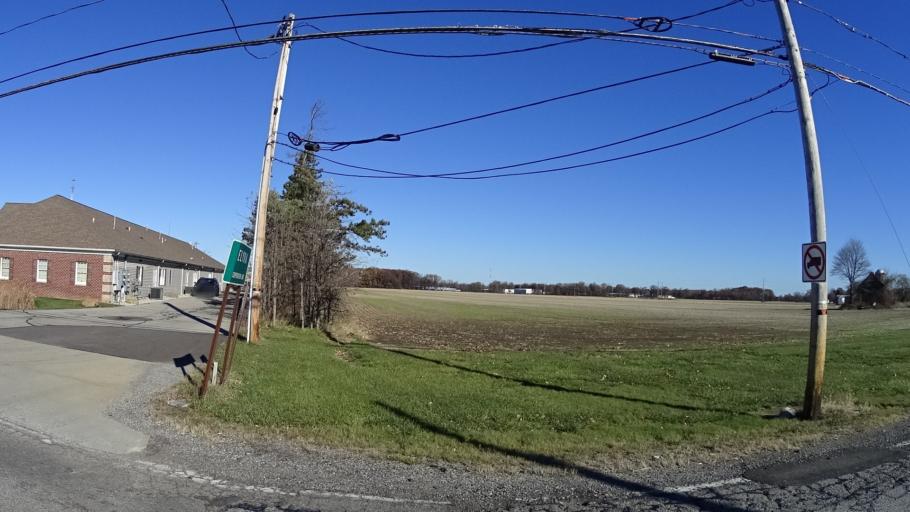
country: US
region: Ohio
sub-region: Lorain County
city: Elyria
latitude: 41.3624
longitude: -82.0691
